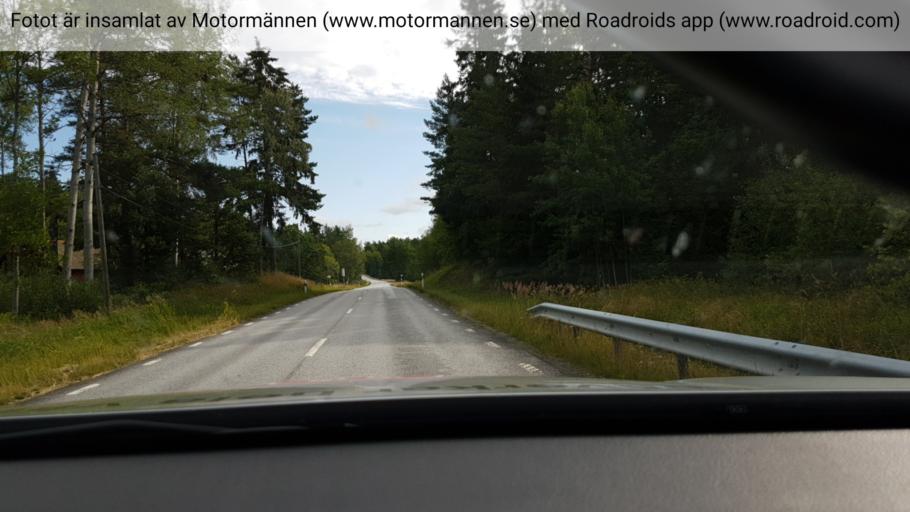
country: SE
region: Stockholm
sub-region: Vaxholms Kommun
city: Resaro
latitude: 59.5456
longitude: 18.4809
